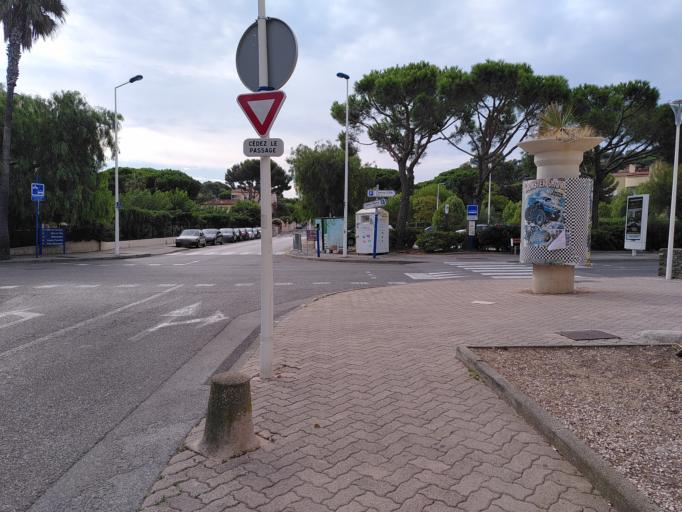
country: FR
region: Provence-Alpes-Cote d'Azur
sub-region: Departement du Var
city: Cavalaire-sur-Mer
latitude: 43.1706
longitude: 6.5327
